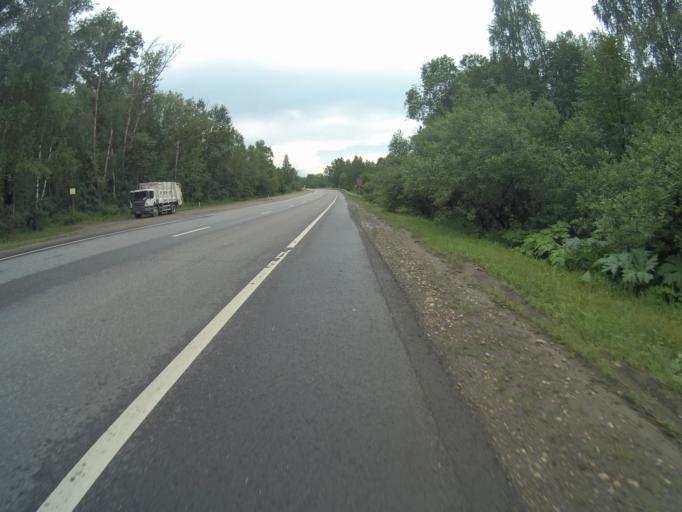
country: RU
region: Vladimir
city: Kameshkovo
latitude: 56.1959
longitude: 40.8819
